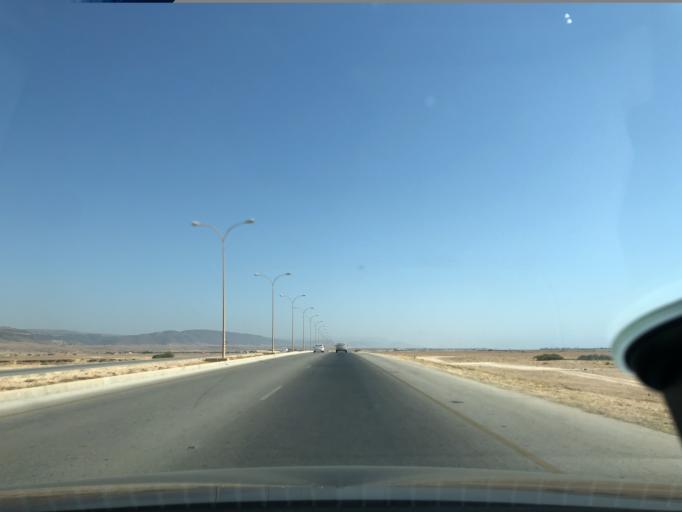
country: OM
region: Zufar
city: Salalah
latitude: 17.0509
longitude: 54.2537
